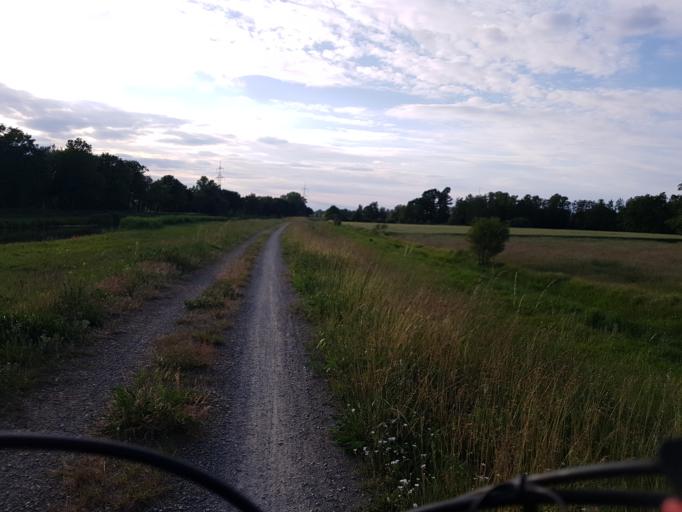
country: DE
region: Brandenburg
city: Bad Liebenwerda
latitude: 51.4932
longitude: 13.4247
